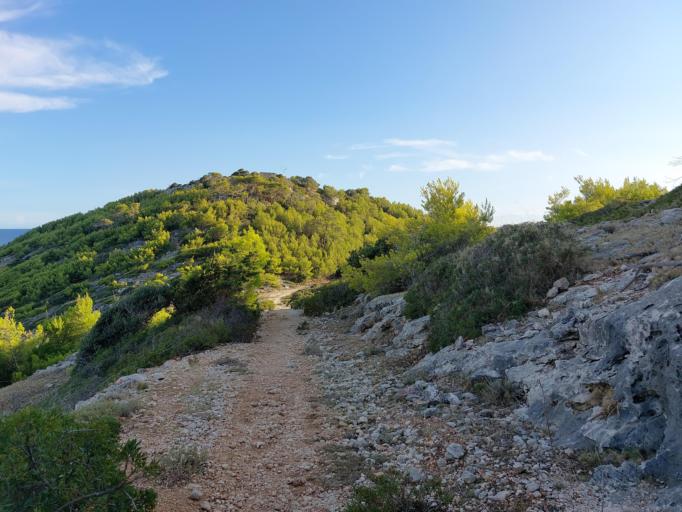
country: HR
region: Dubrovacko-Neretvanska
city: Smokvica
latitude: 42.7272
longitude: 16.8450
